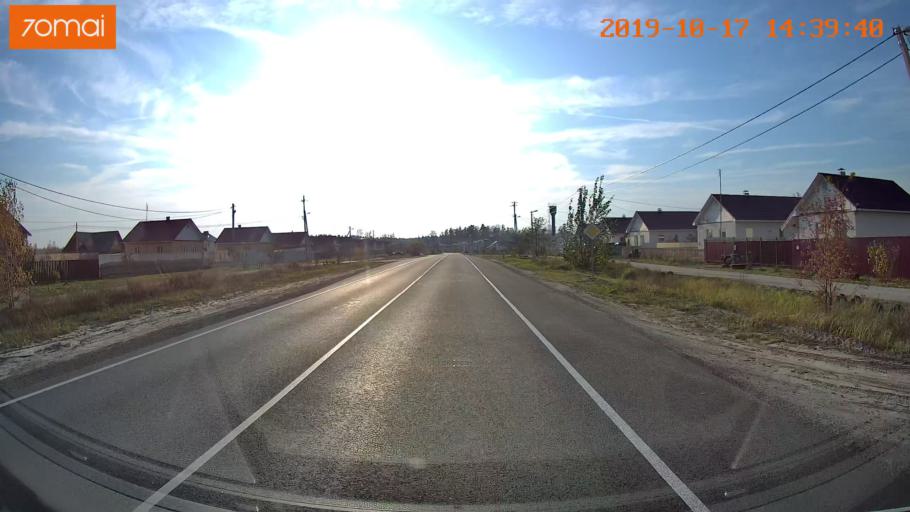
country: RU
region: Rjazan
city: Solotcha
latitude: 54.8606
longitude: 39.9665
